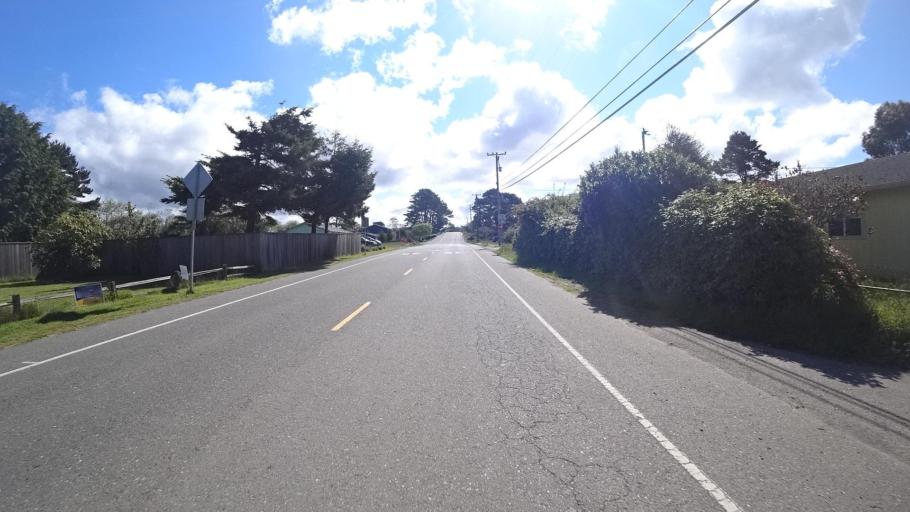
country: US
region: California
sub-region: Humboldt County
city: McKinleyville
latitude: 40.9417
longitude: -124.1193
